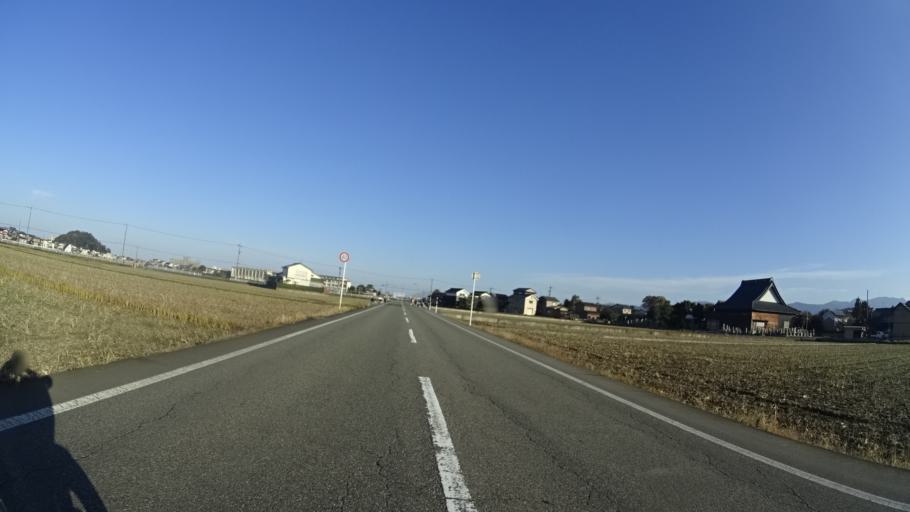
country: JP
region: Fukui
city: Fukui-shi
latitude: 36.0693
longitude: 136.2570
